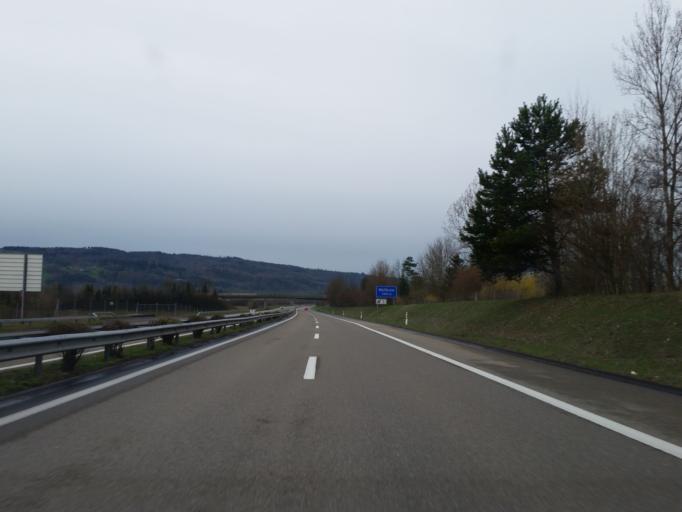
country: CH
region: Thurgau
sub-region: Frauenfeld District
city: Mullheim
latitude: 47.5997
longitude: 9.0134
